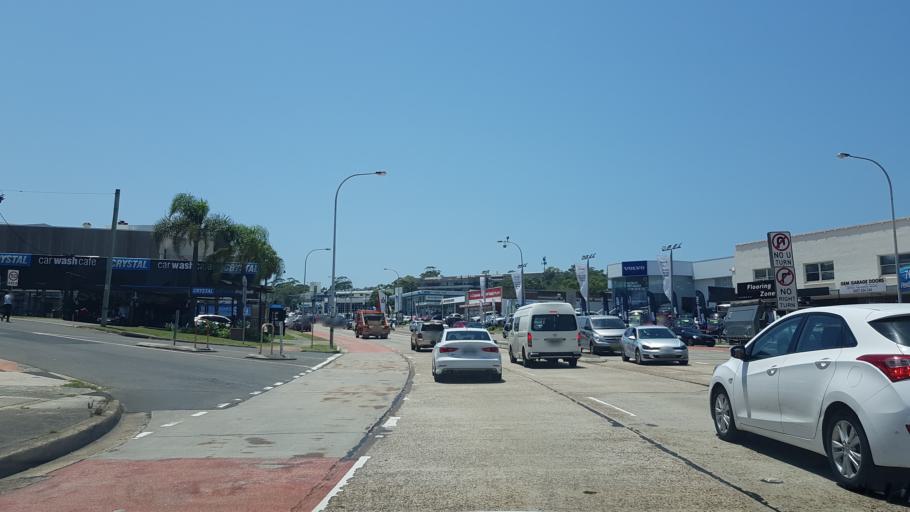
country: AU
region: New South Wales
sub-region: Warringah
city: Brookvale
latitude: -33.7611
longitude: 151.2768
